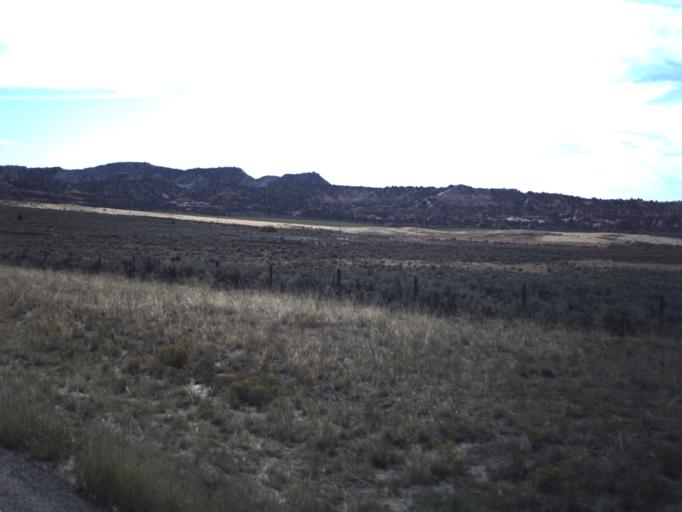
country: US
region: Utah
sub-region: Garfield County
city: Panguitch
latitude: 37.5615
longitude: -112.0291
